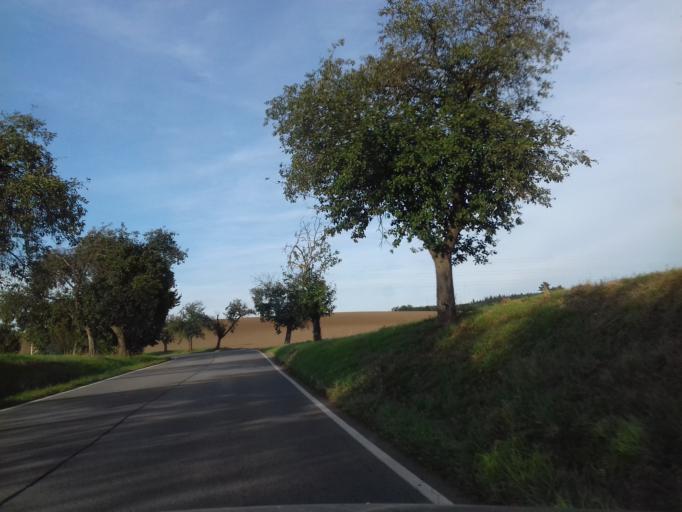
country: CZ
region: Central Bohemia
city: Kamenny Privoz
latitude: 49.8684
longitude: 14.5045
